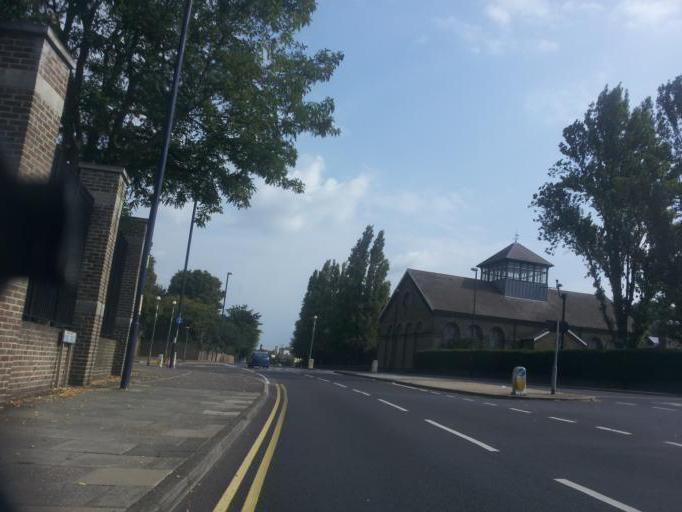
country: GB
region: England
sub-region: Kent
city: Chatham
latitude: 51.3923
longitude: 0.5328
